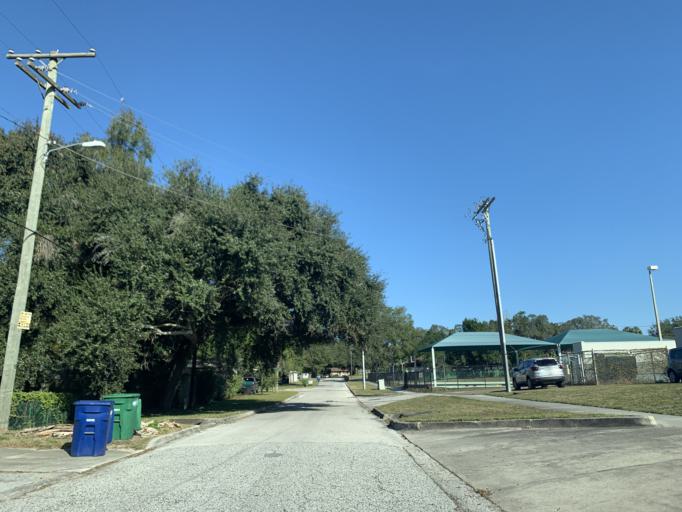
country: US
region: Florida
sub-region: Hillsborough County
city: Temple Terrace
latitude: 28.0268
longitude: -82.4110
